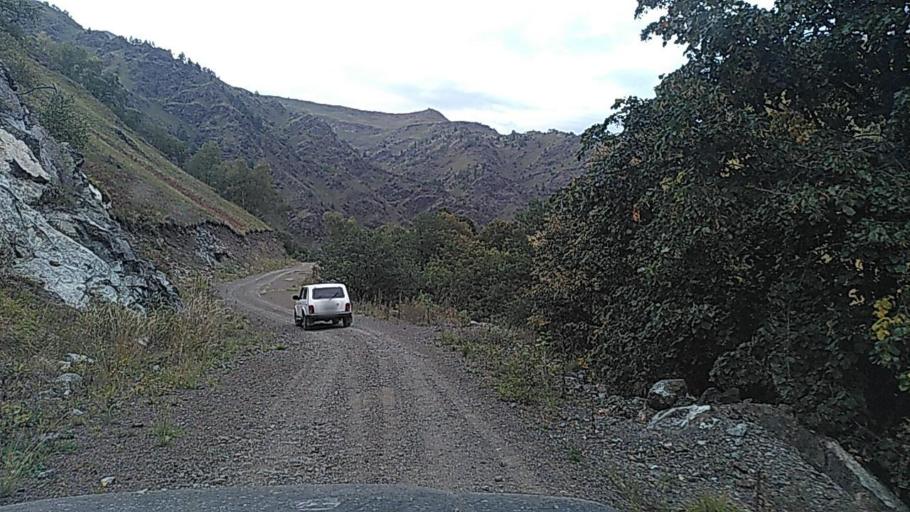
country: RU
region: Kabardino-Balkariya
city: Kamennomostskoye
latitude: 43.7158
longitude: 42.8455
